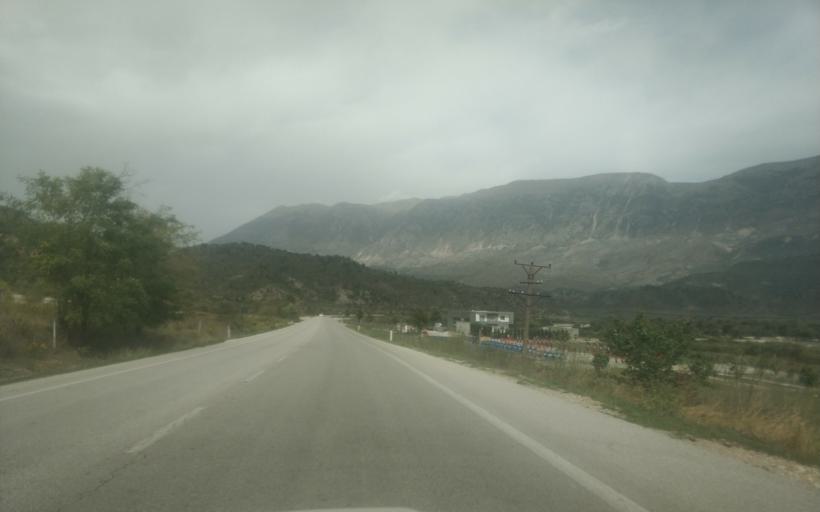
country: AL
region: Gjirokaster
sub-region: Rrethi i Gjirokastres
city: Picar
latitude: 40.1901
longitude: 20.0813
